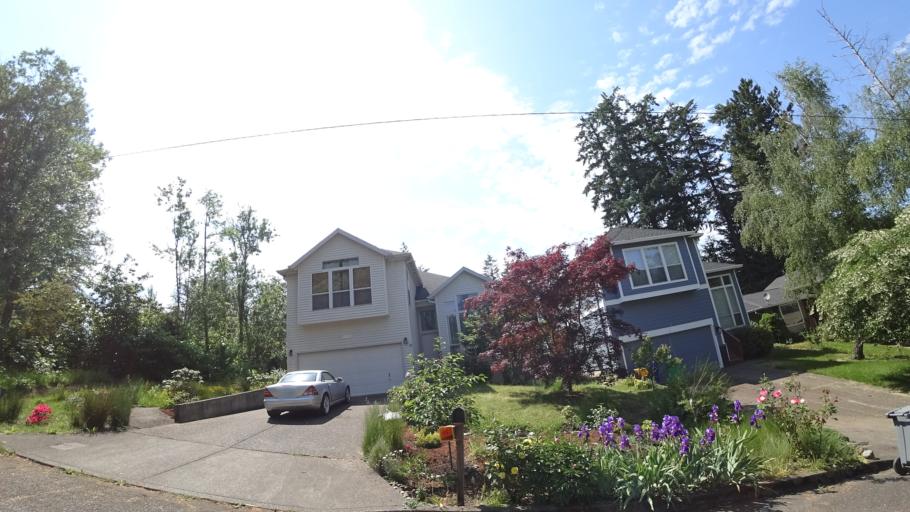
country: US
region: Oregon
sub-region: Washington County
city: Garden Home-Whitford
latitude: 45.4563
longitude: -122.7324
